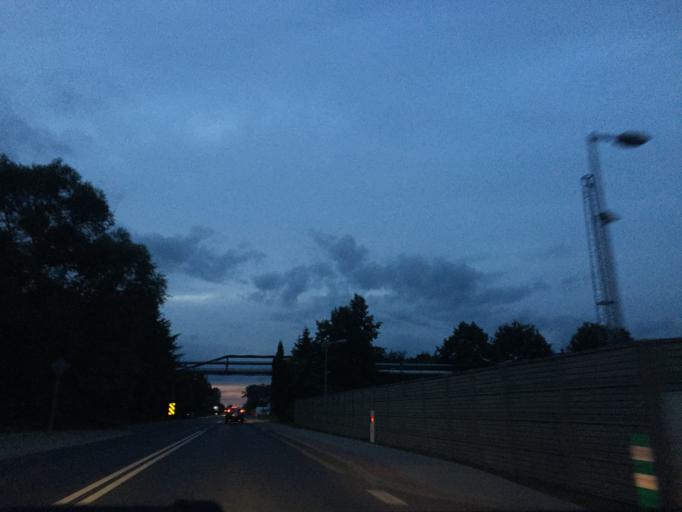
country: PL
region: Lesser Poland Voivodeship
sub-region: Powiat oswiecimski
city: Zaborze
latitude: 50.0258
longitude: 19.2531
